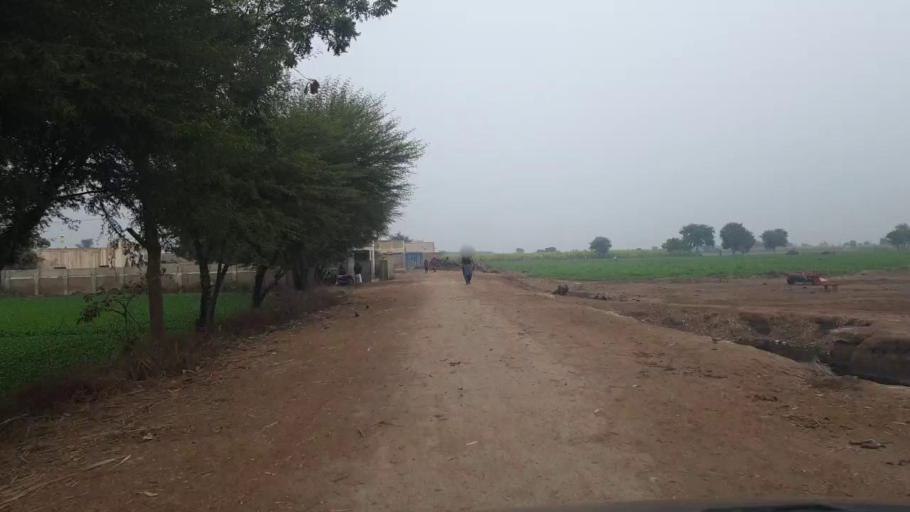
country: PK
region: Sindh
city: Tando Adam
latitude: 25.8036
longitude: 68.6875
